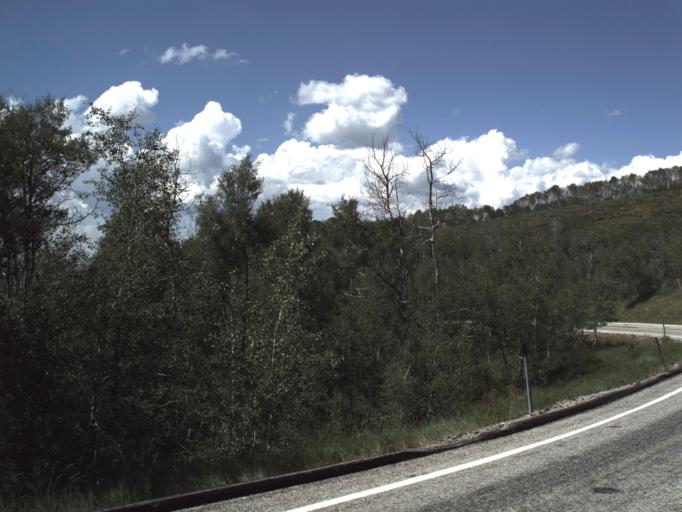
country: US
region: Utah
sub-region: Weber County
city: Wolf Creek
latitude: 41.4114
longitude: -111.5592
